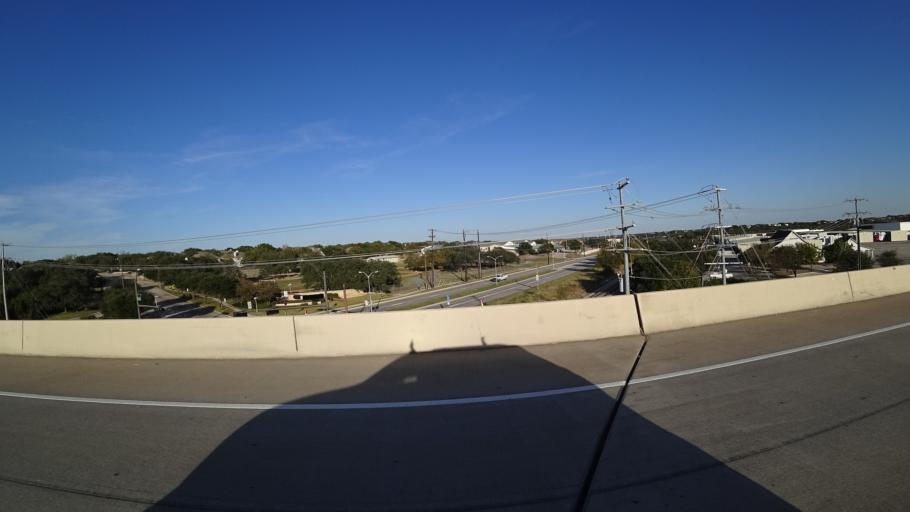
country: US
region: Texas
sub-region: Williamson County
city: Cedar Park
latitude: 30.5028
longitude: -97.8083
